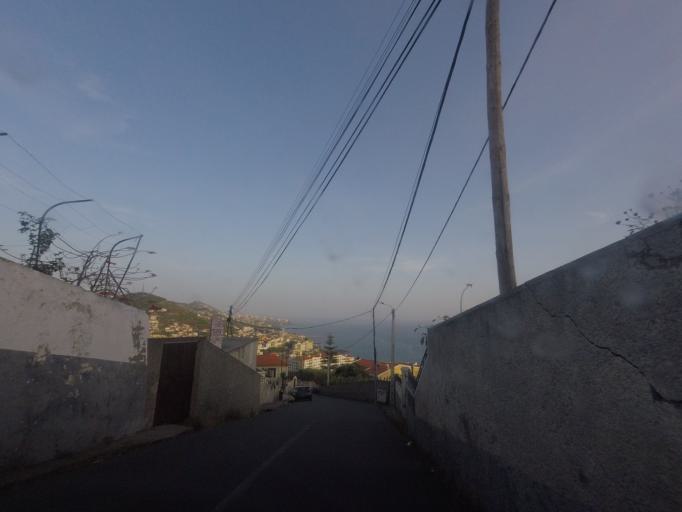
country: PT
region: Madeira
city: Camara de Lobos
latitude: 32.6537
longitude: -16.9872
